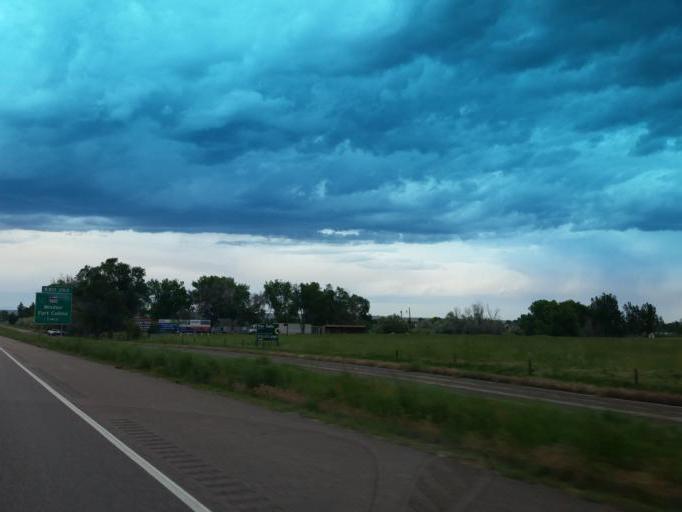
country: US
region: Colorado
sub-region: Weld County
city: Windsor
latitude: 40.4619
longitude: -104.9918
